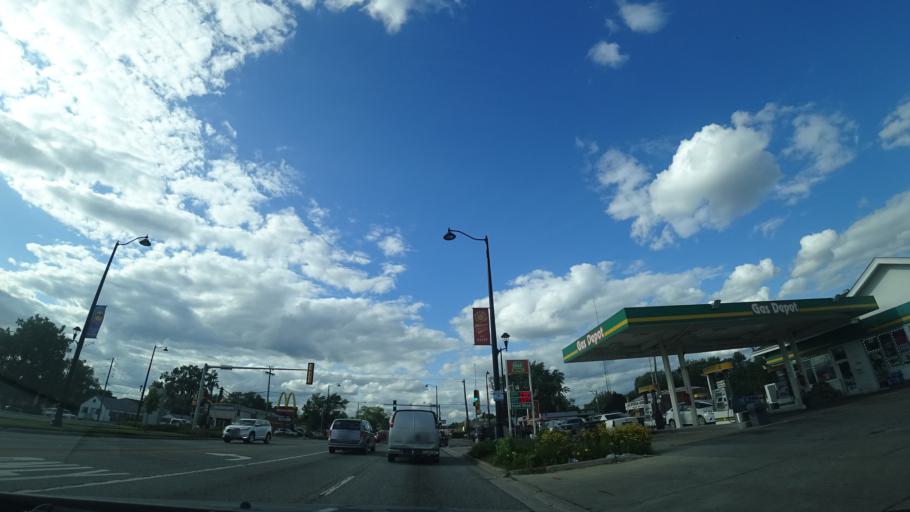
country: US
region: Illinois
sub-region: Cook County
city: Alsip
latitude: 41.6762
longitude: -87.7196
